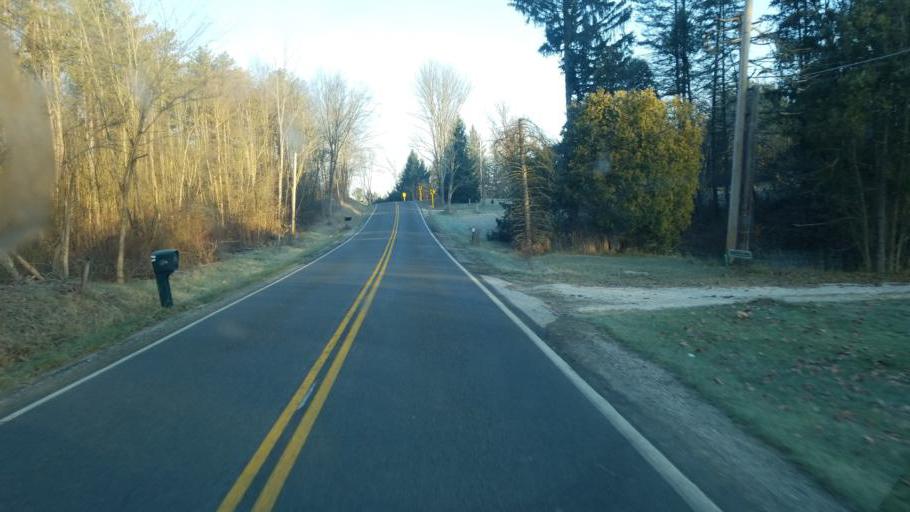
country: US
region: Ohio
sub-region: Medina County
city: Medina
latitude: 41.1008
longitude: -81.8040
